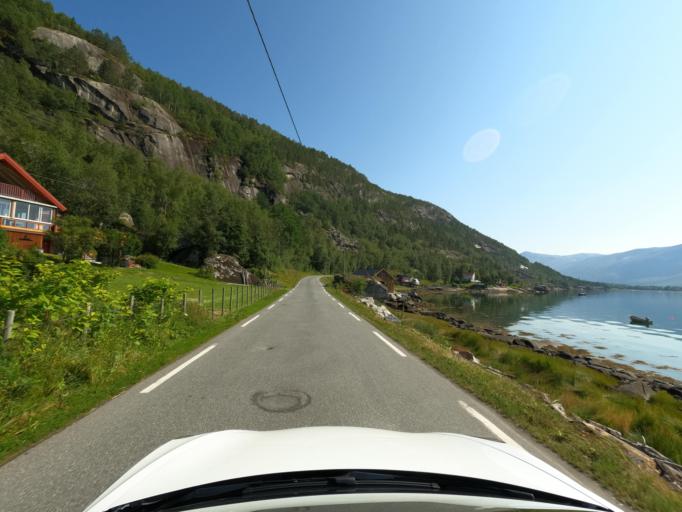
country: NO
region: Nordland
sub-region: Narvik
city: Narvik
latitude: 68.2749
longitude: 17.3959
